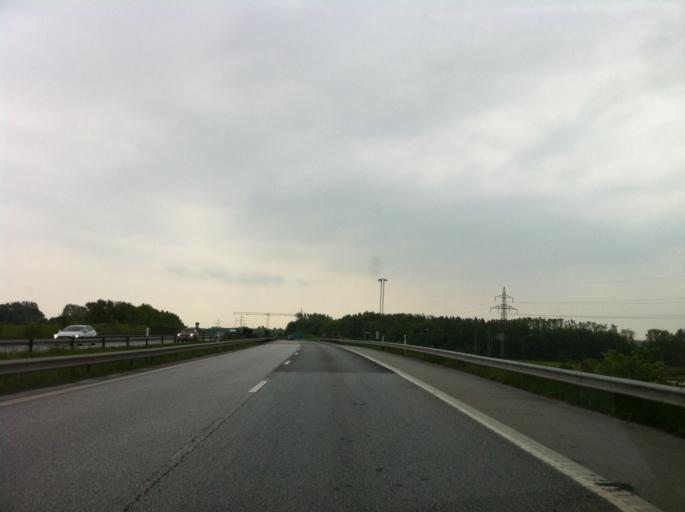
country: SE
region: Skane
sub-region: Burlovs Kommun
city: Arloev
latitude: 55.6525
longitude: 13.0980
